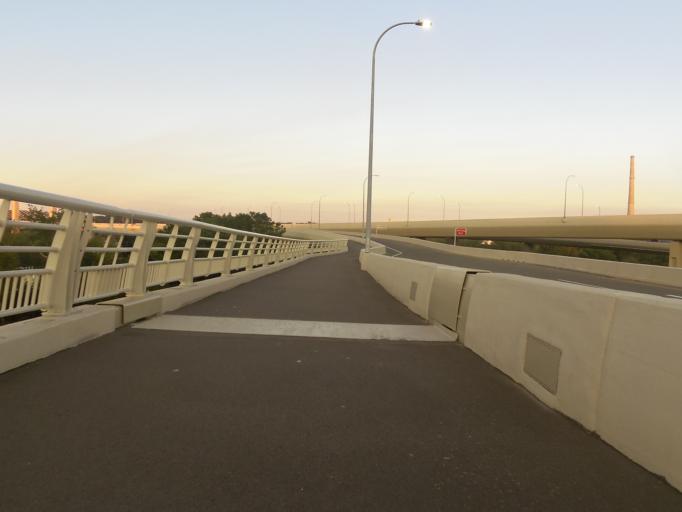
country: US
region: Minnesota
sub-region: Washington County
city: Oak Park Heights
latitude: 45.0370
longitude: -92.7930
